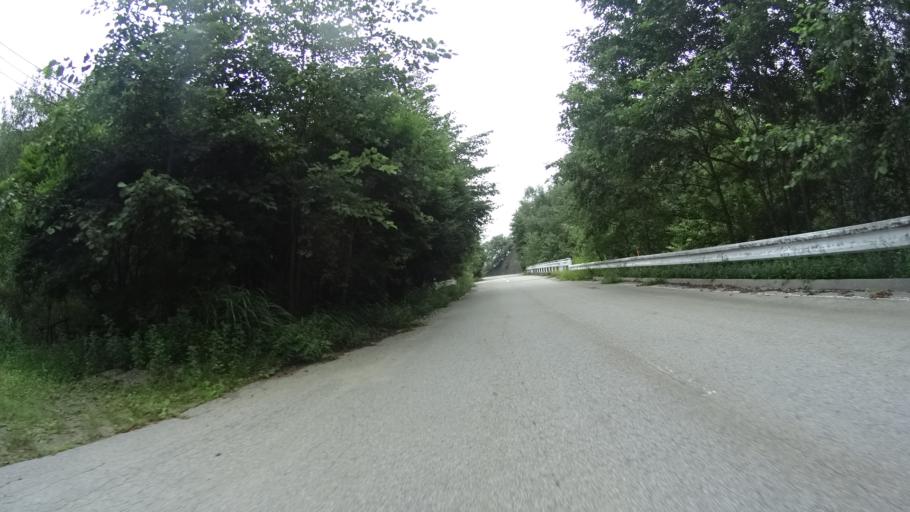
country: JP
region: Yamanashi
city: Enzan
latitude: 35.8067
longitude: 138.6623
